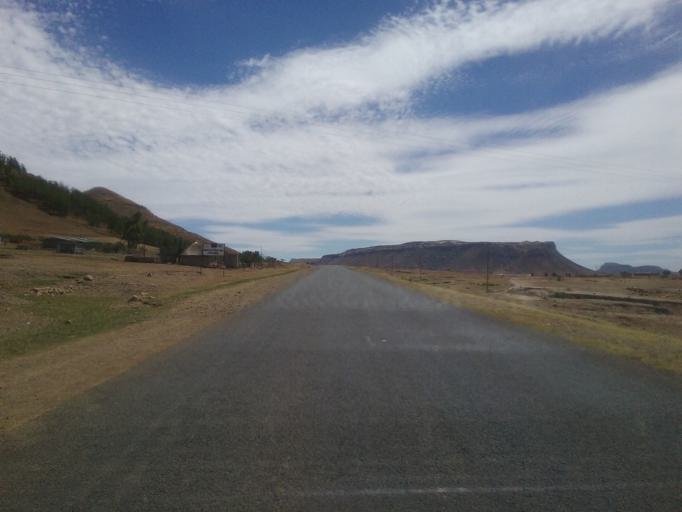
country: LS
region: Mafeteng
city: Mafeteng
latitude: -29.9164
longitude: 27.2484
